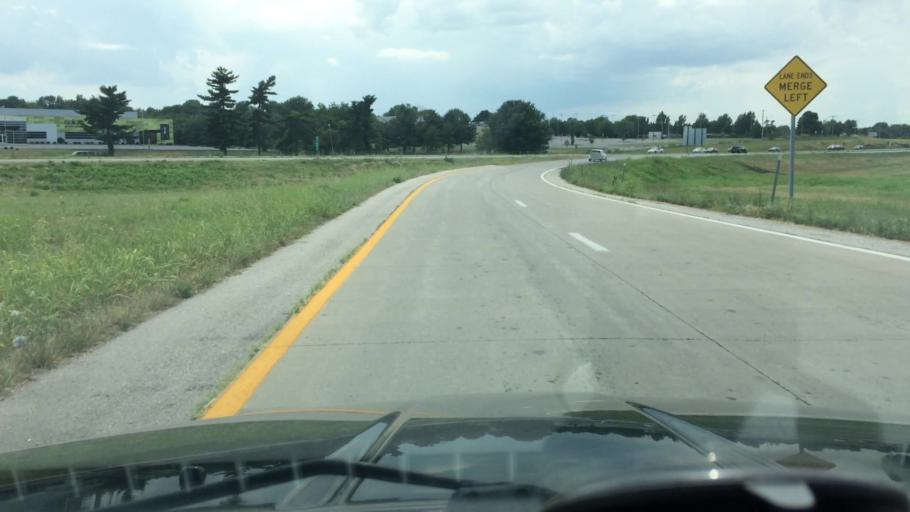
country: US
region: Missouri
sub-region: Greene County
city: Springfield
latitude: 37.2511
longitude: -93.2657
